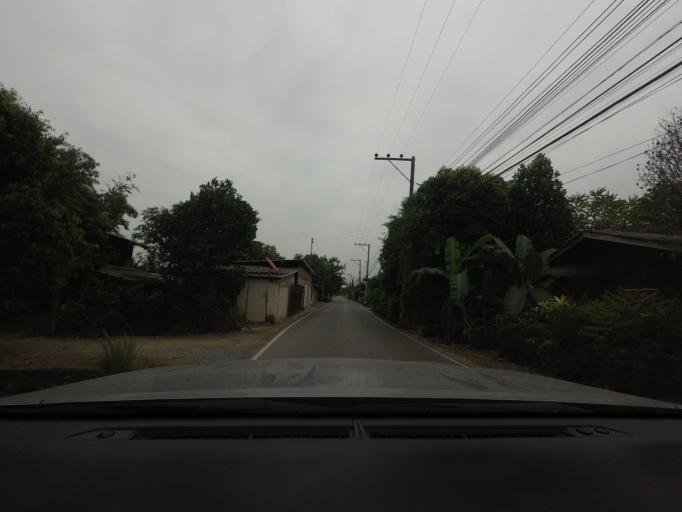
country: TH
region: Lamphun
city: Lamphun
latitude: 18.6290
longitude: 99.0156
